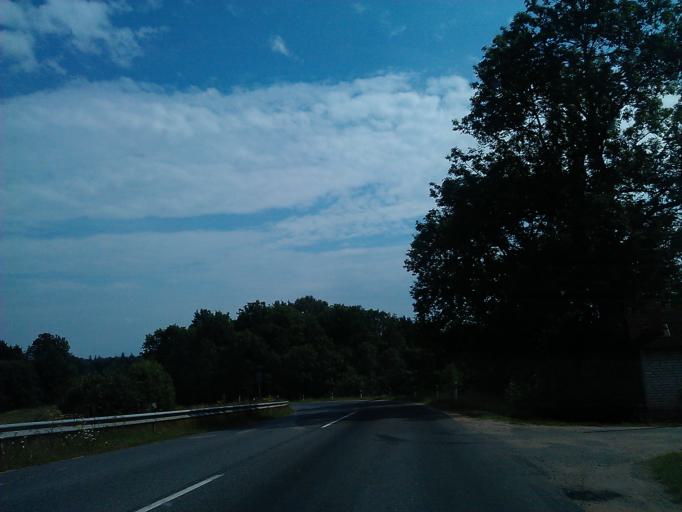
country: LV
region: Priekuli
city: Priekuli
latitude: 57.3339
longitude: 25.3237
